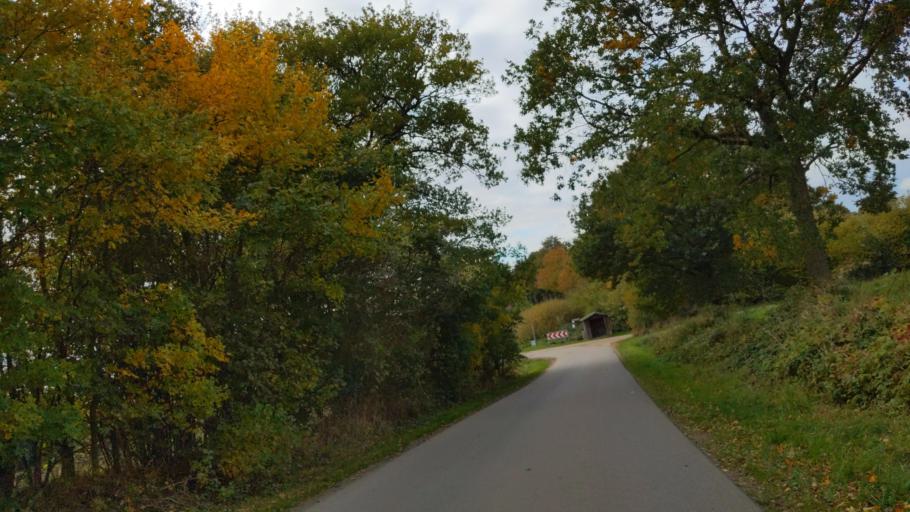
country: DE
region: Schleswig-Holstein
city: Sierksdorf
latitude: 54.0962
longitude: 10.7596
